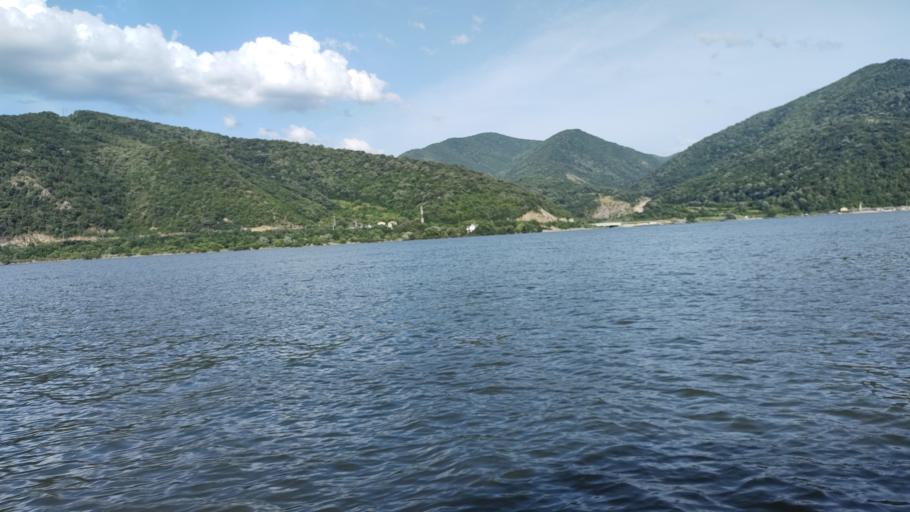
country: RO
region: Caras-Severin
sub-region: Comuna Berzasca
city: Berzasca
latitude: 44.6243
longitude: 21.9968
